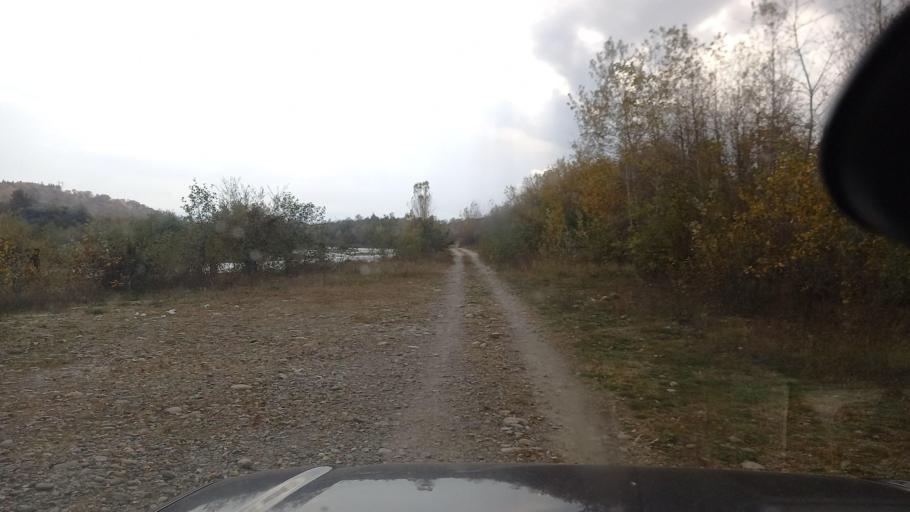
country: RU
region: Krasnodarskiy
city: Shedok
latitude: 44.1753
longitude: 40.8500
